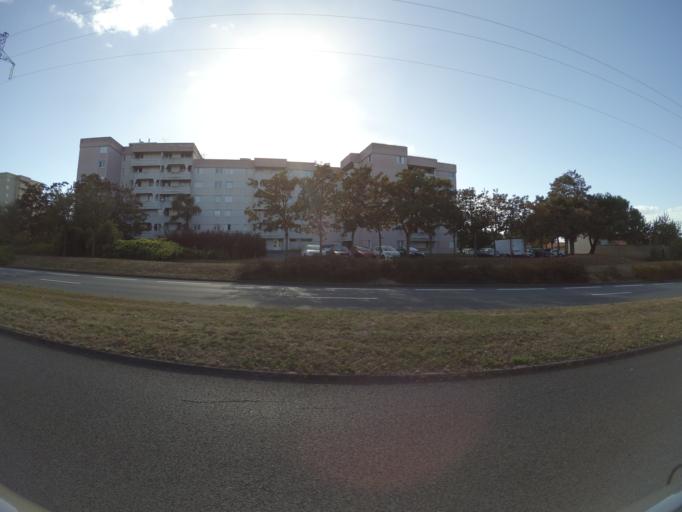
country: FR
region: Pays de la Loire
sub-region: Departement de Maine-et-Loire
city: Cholet
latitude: 47.0516
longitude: -0.8994
